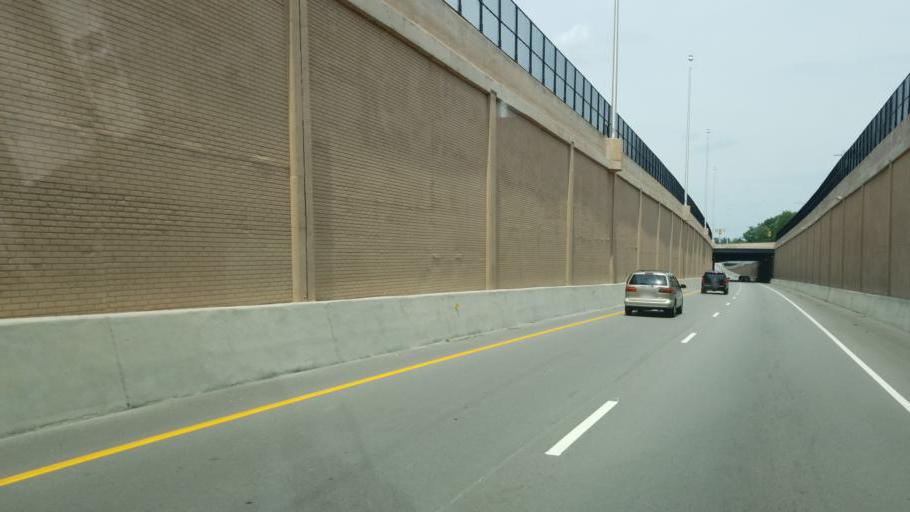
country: US
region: Ohio
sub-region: Franklin County
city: Worthington
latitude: 40.1205
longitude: -83.0160
